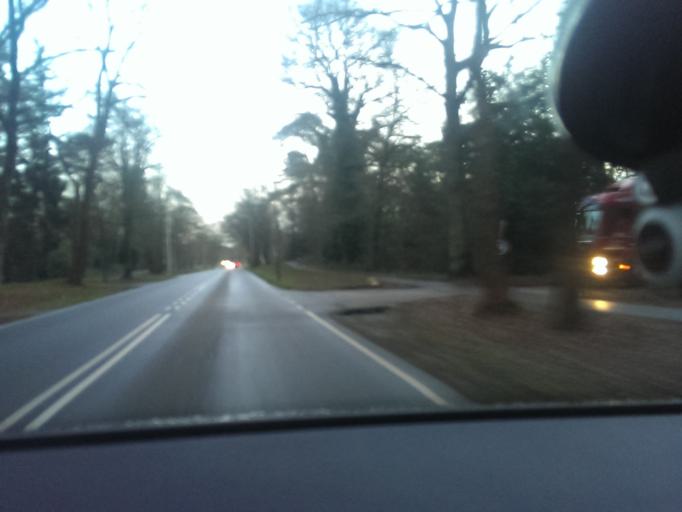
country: NL
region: Overijssel
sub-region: Gemeente Twenterand
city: Den Ham
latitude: 52.5035
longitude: 6.4214
